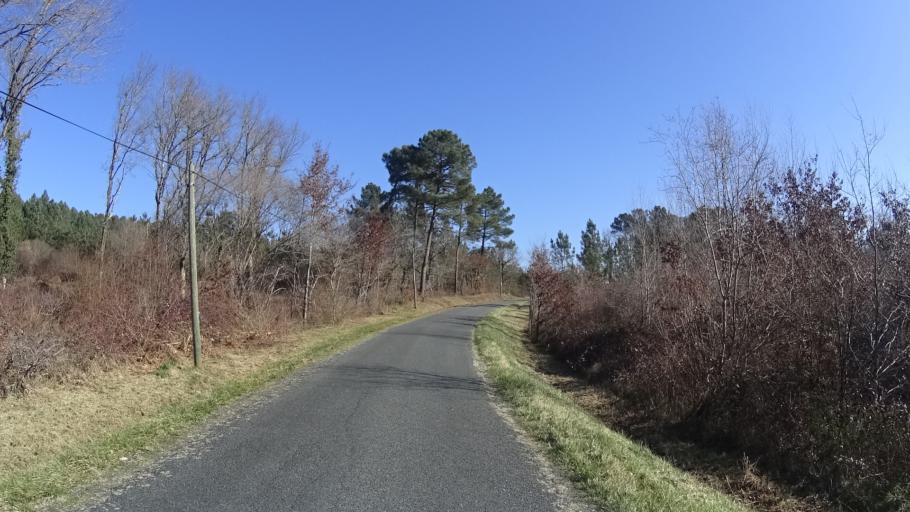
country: FR
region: Aquitaine
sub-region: Departement de la Dordogne
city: Saint-Aulaye
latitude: 45.1211
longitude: 0.2081
